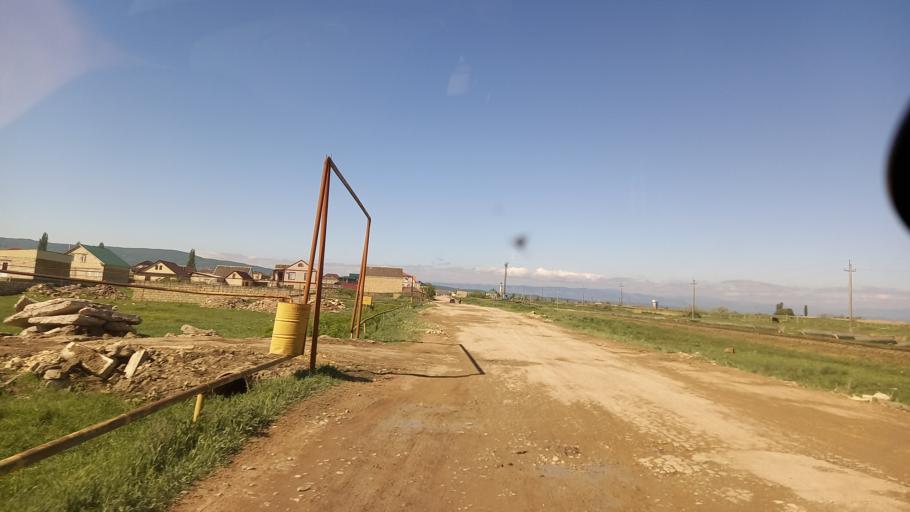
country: RU
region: Dagestan
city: Dagestanskiye Ogni
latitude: 42.1282
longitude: 48.2214
